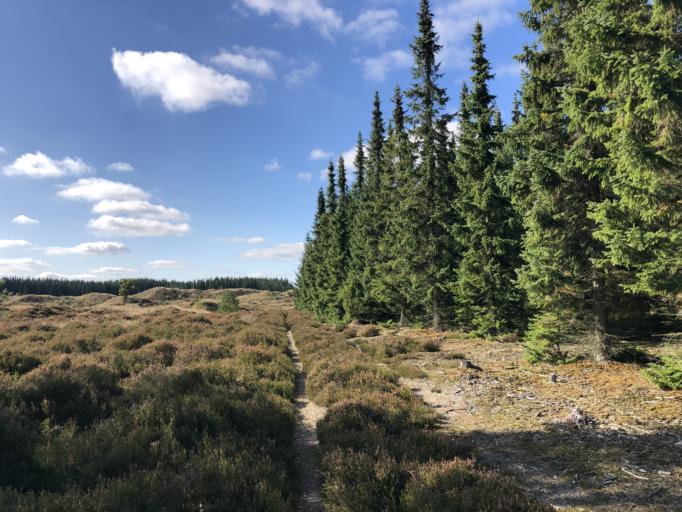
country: DK
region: Central Jutland
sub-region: Holstebro Kommune
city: Holstebro
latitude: 56.2495
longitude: 8.4953
